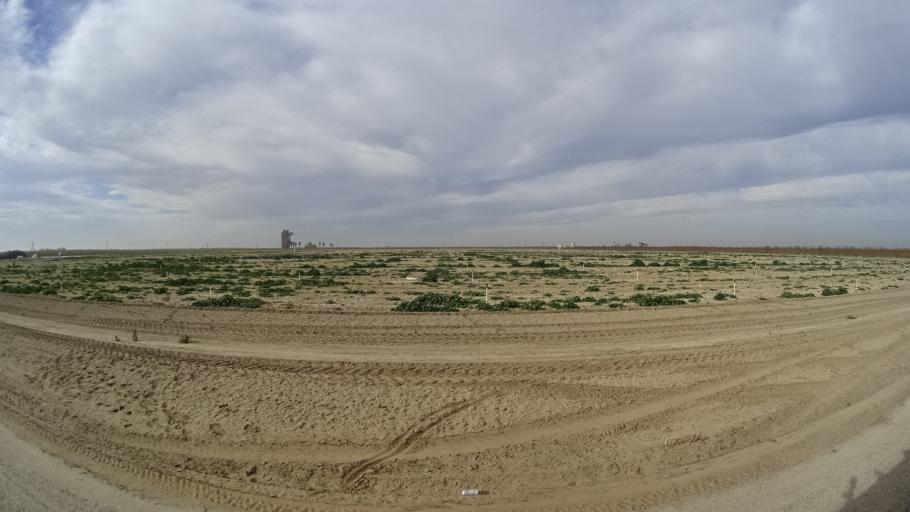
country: US
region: California
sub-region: Kern County
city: Rosedale
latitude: 35.4079
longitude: -119.1722
